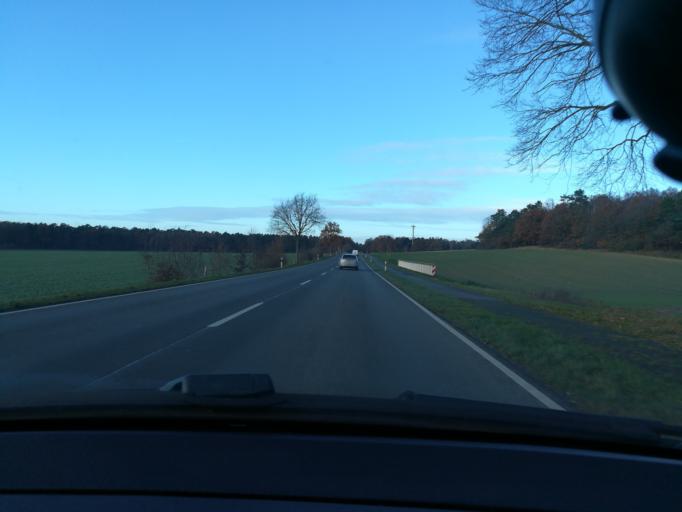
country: DE
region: Lower Saxony
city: Kirchdorf
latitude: 52.5728
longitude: 8.8458
